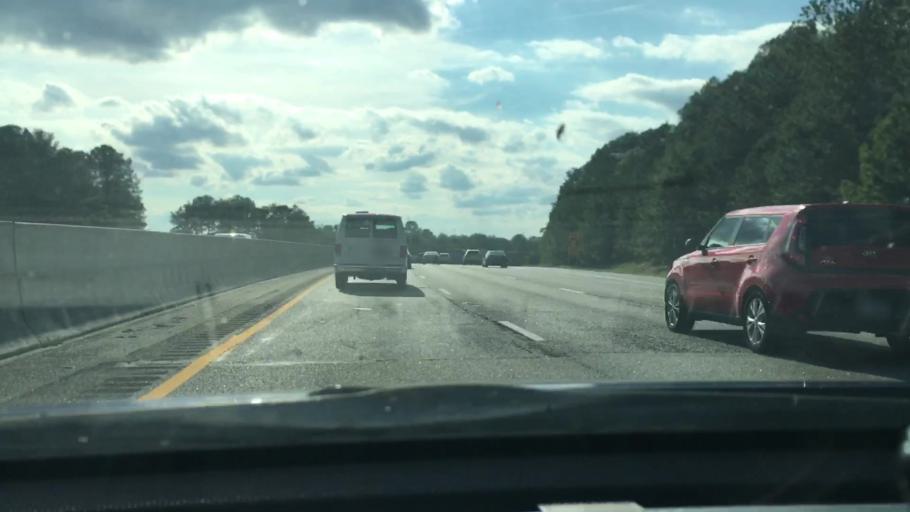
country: US
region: South Carolina
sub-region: Richland County
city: Forest Acres
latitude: 34.0677
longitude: -81.0189
